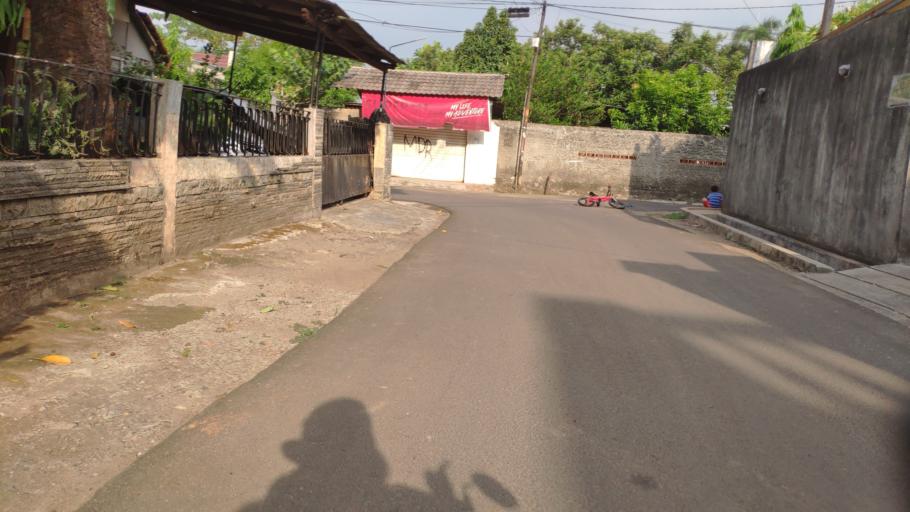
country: ID
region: West Java
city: Pamulang
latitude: -6.3004
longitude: 106.8030
